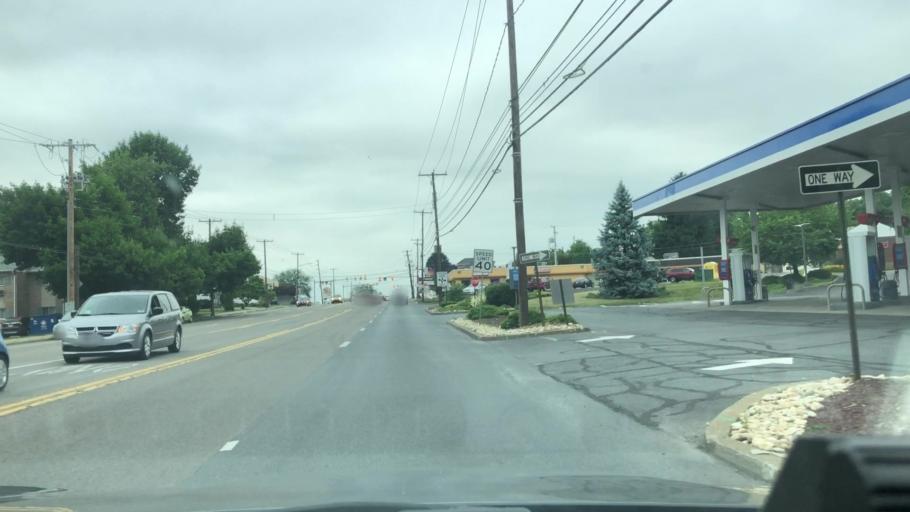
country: US
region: Pennsylvania
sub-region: Northampton County
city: Bethlehem
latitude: 40.6386
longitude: -75.3978
